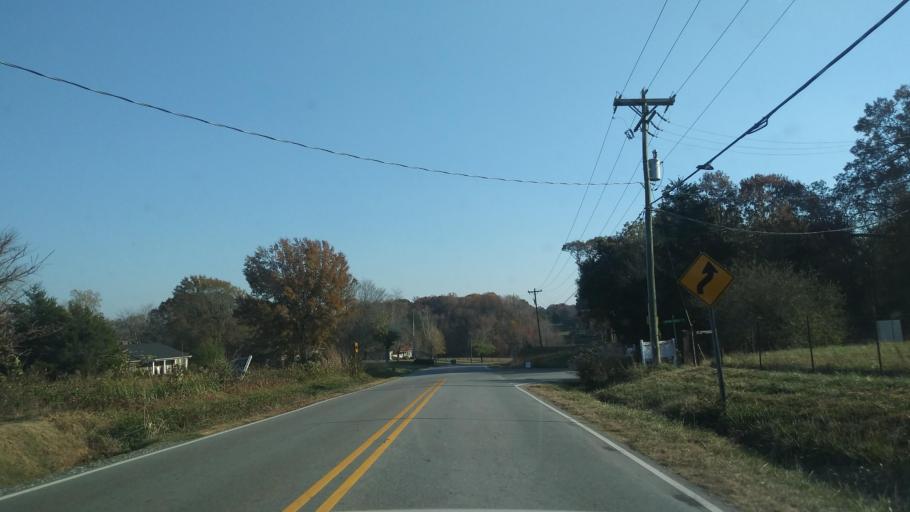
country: US
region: North Carolina
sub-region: Guilford County
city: McLeansville
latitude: 36.2087
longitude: -79.7145
